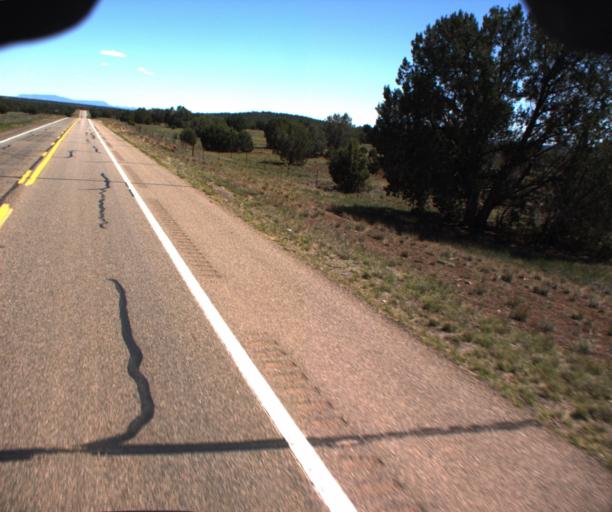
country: US
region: Arizona
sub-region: Yavapai County
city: Paulden
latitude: 35.1475
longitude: -112.4480
